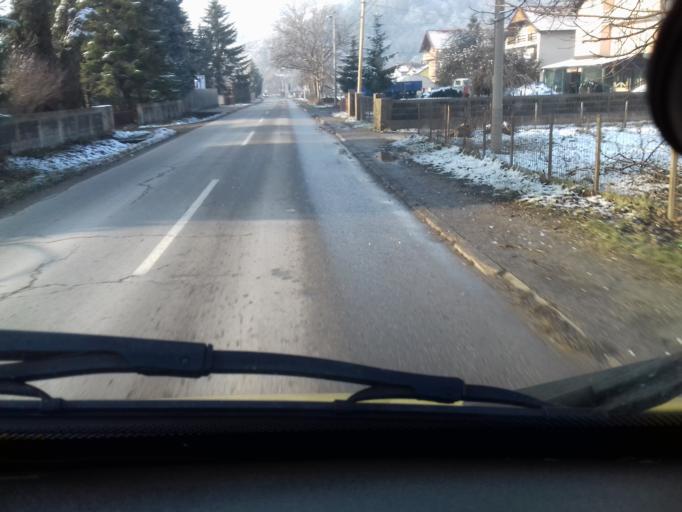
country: BA
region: Federation of Bosnia and Herzegovina
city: Mahala
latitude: 43.9959
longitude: 18.2194
